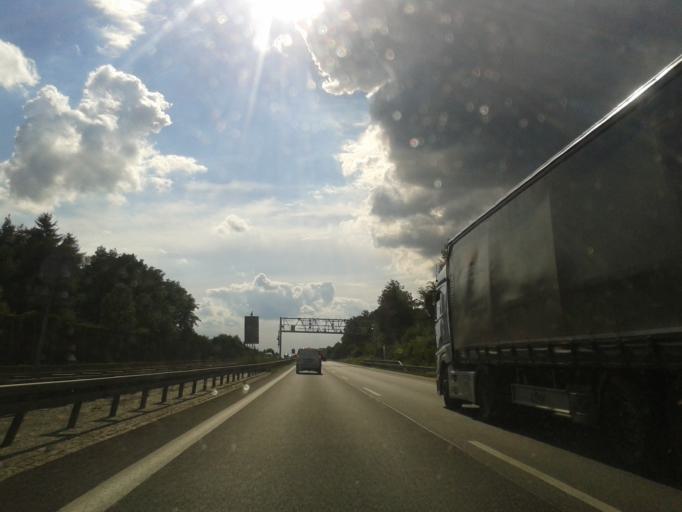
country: DE
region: Saxony
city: Hauswalde
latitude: 51.1711
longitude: 14.0784
